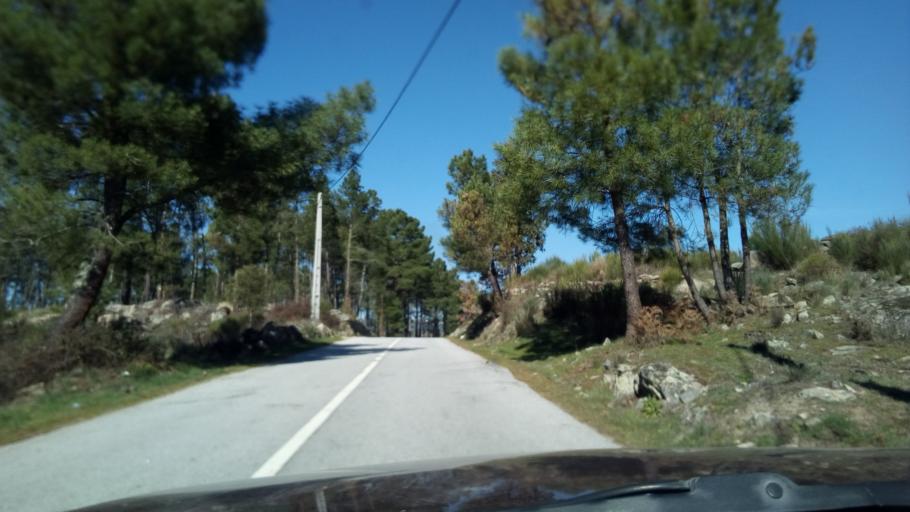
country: PT
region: Guarda
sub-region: Fornos de Algodres
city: Fornos de Algodres
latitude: 40.5901
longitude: -7.5097
